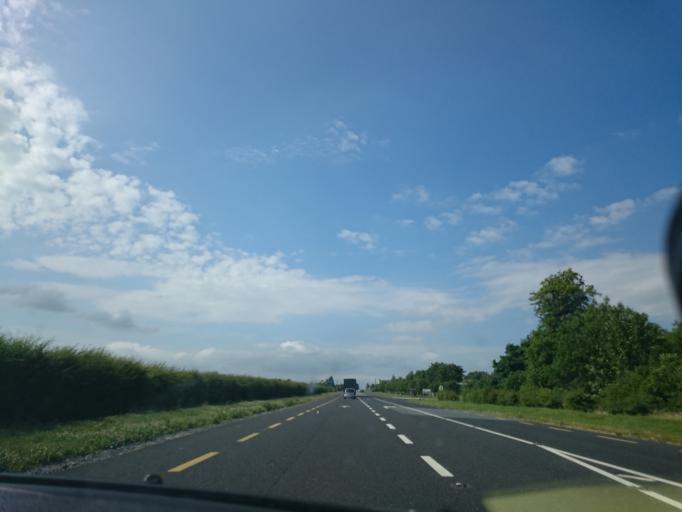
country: IE
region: Leinster
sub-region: Kilkenny
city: Kilkenny
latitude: 52.5796
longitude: -7.2369
